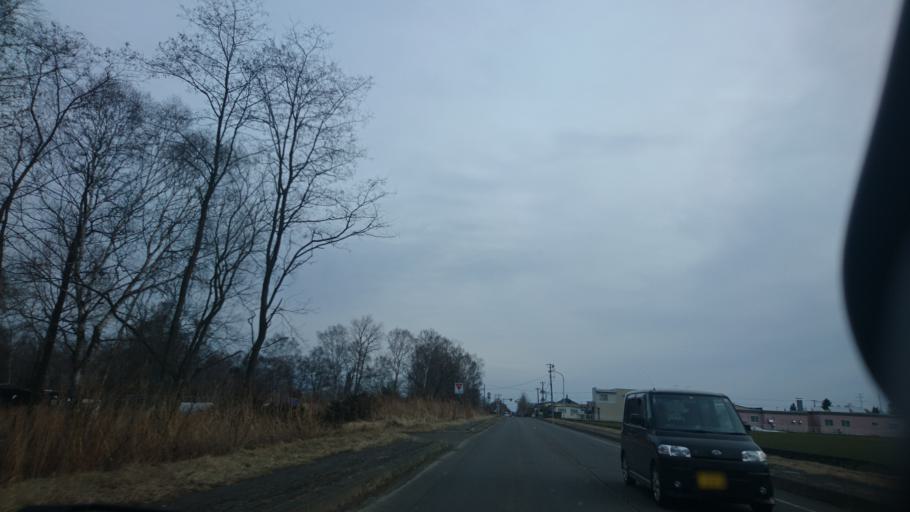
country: JP
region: Hokkaido
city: Otofuke
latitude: 42.9738
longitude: 143.1985
